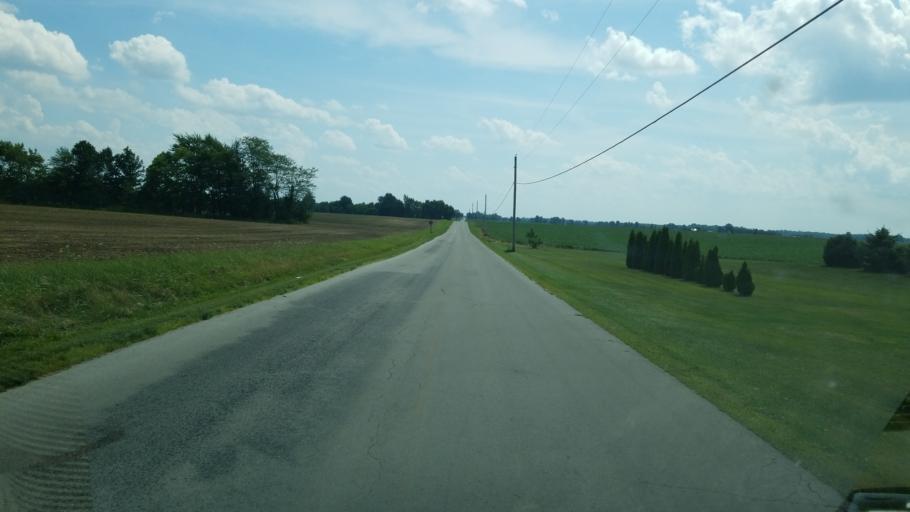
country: US
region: Ohio
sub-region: Hardin County
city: Forest
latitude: 40.8609
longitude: -83.4770
